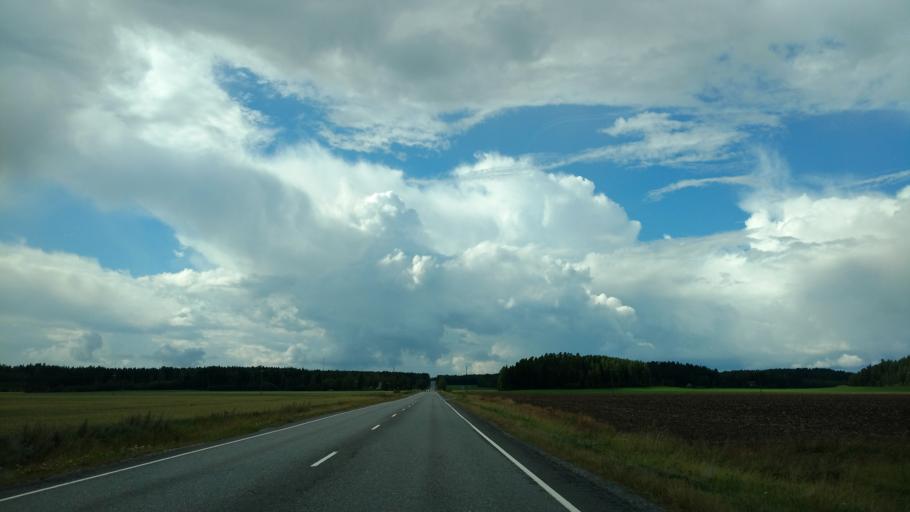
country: FI
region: Varsinais-Suomi
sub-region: Turku
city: Sauvo
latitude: 60.3930
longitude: 22.8618
